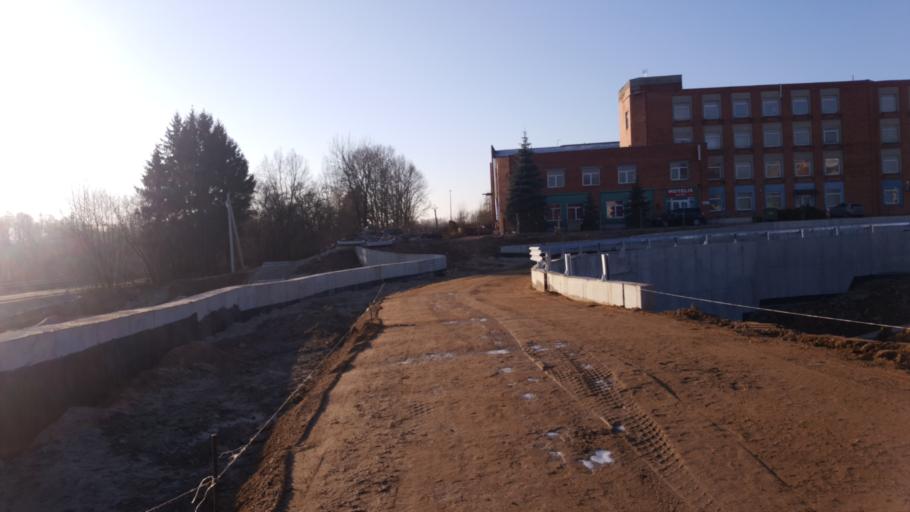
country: LT
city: Ramuciai
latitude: 54.9005
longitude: 24.0326
